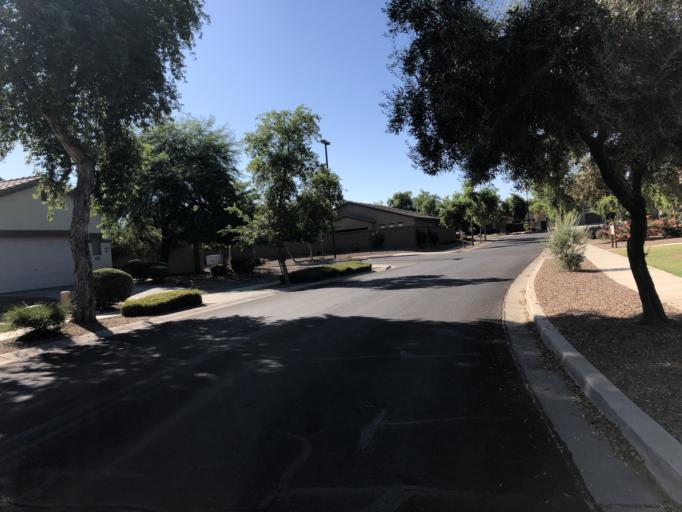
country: US
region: Arizona
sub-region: Maricopa County
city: Queen Creek
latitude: 33.2664
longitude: -111.6987
